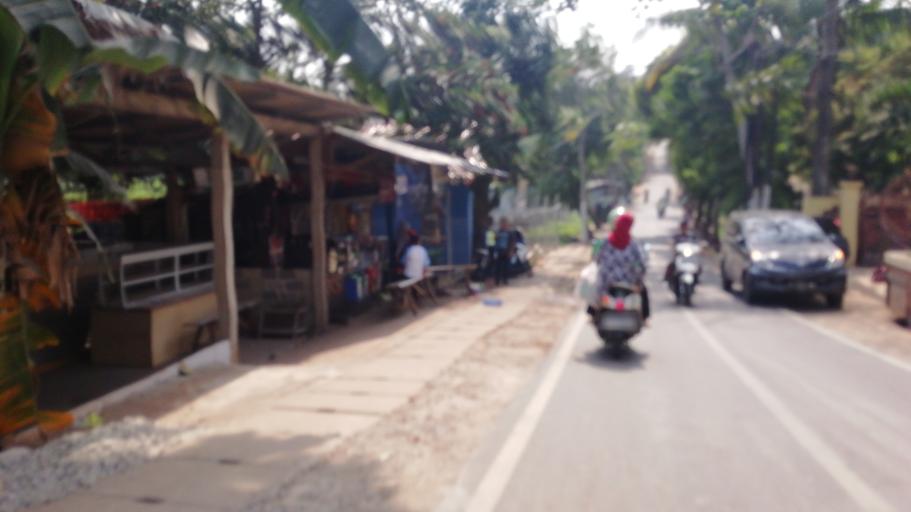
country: ID
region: West Java
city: Depok
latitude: -6.3517
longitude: 106.7981
